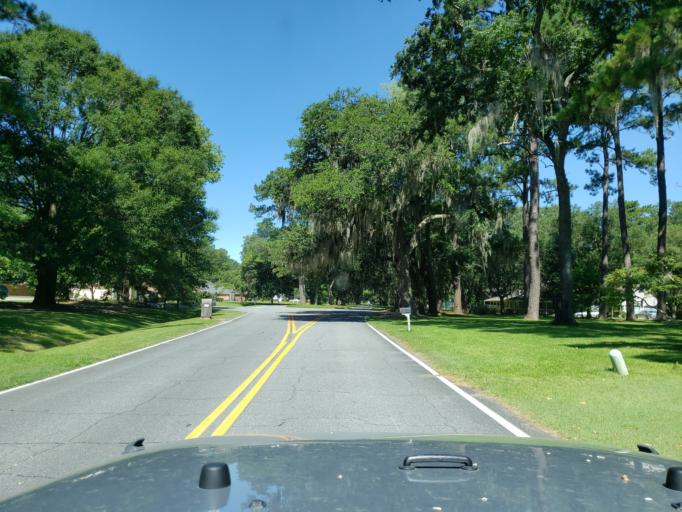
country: US
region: Georgia
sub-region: Chatham County
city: Georgetown
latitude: 31.9711
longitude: -81.2227
